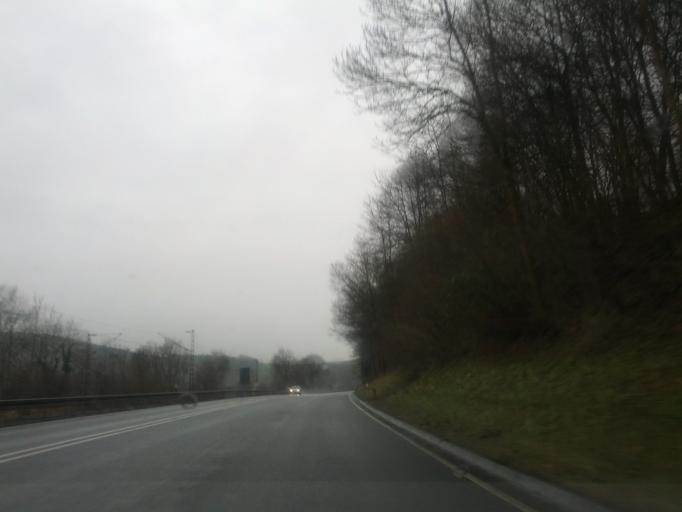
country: DE
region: Hesse
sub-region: Regierungsbezirk Kassel
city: Bad Sooden-Allendorf
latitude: 51.2354
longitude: 9.9853
